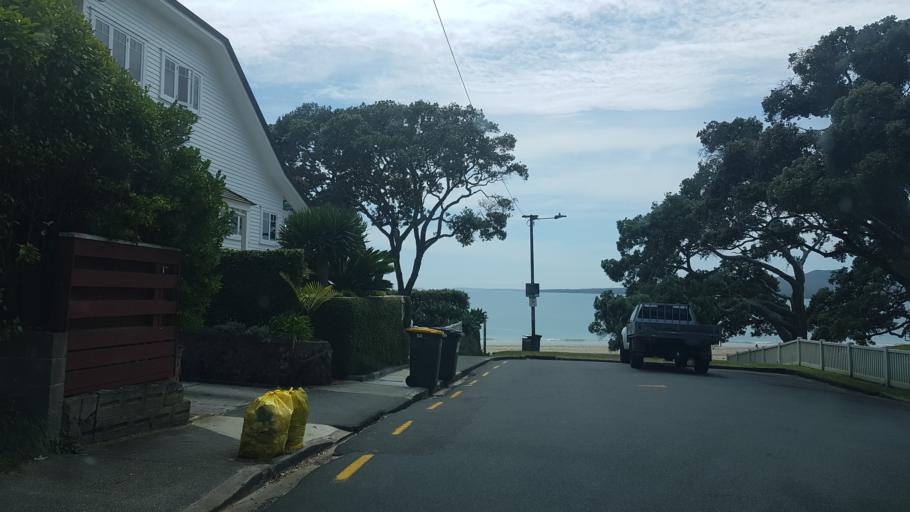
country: NZ
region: Auckland
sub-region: Auckland
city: North Shore
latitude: -36.7913
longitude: 174.7780
